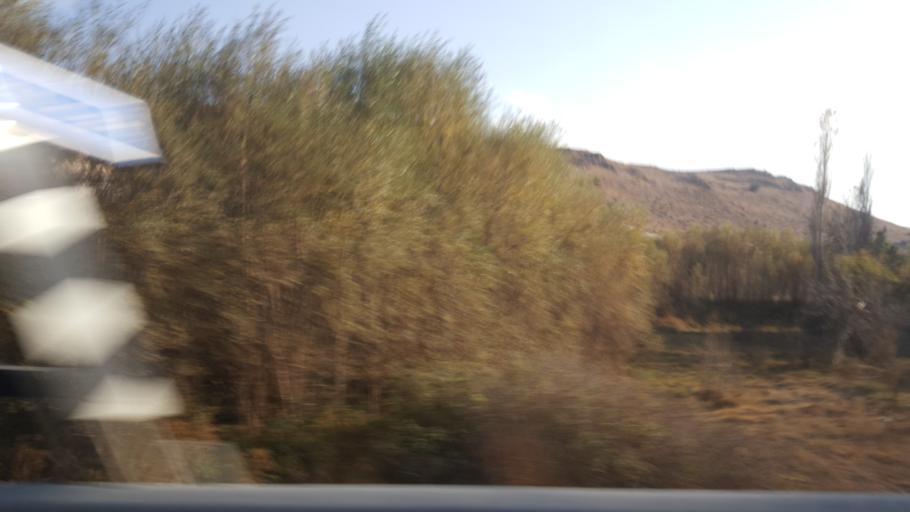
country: TR
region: Eskisehir
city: Seyitgazi
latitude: 39.4162
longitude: 30.6470
